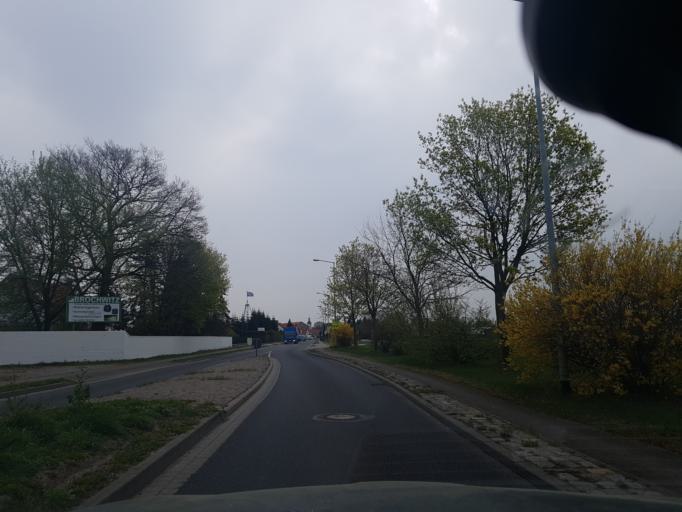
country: DE
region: Brandenburg
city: Plessa
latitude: 51.4647
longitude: 13.6107
